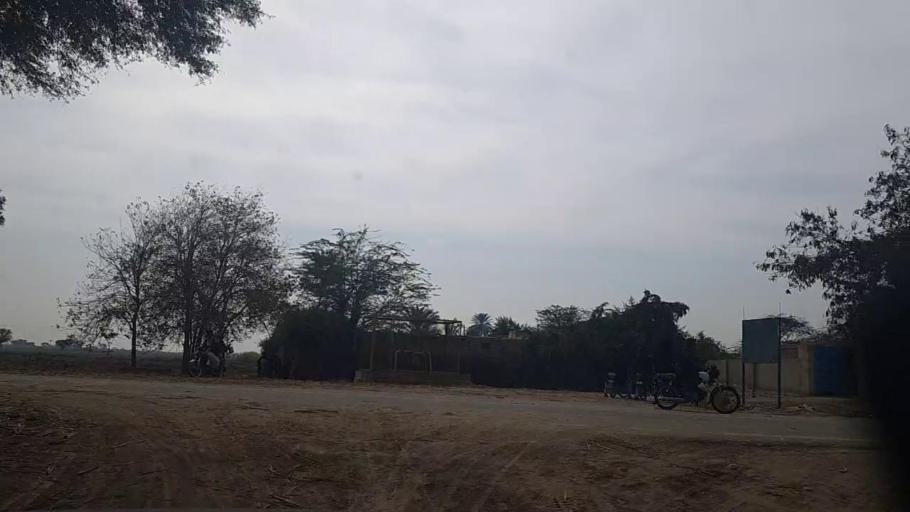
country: PK
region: Sindh
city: Sakrand
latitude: 26.2260
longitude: 68.2970
